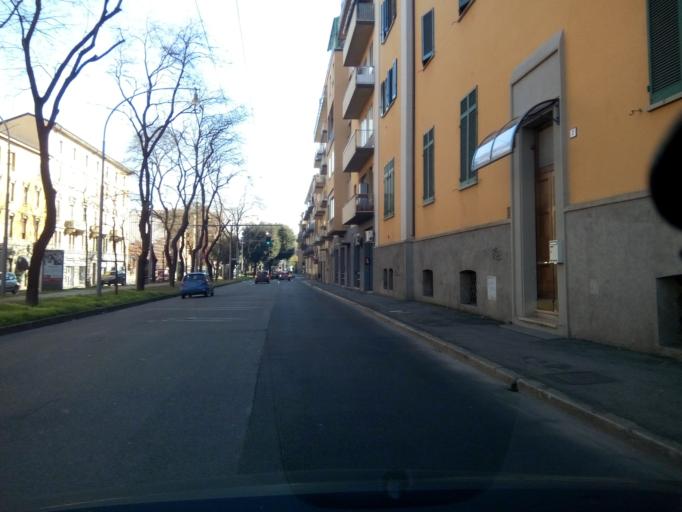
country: IT
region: Emilia-Romagna
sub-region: Provincia di Bologna
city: Bologna
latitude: 44.5015
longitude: 11.3314
